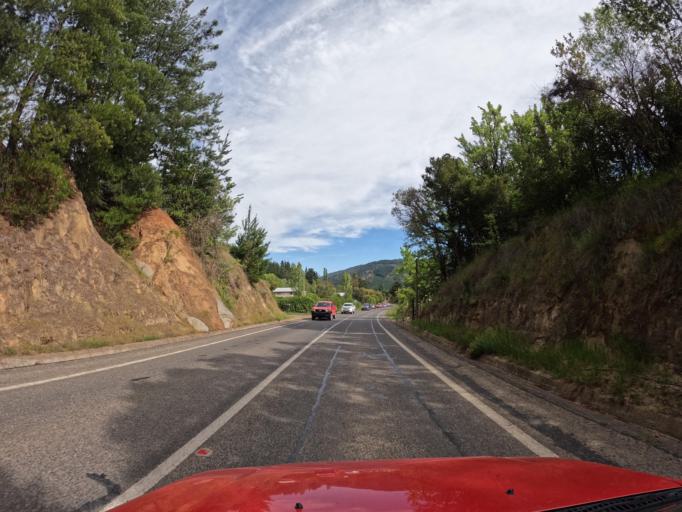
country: CL
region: Maule
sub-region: Provincia de Talca
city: Talca
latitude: -35.3058
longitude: -71.9645
